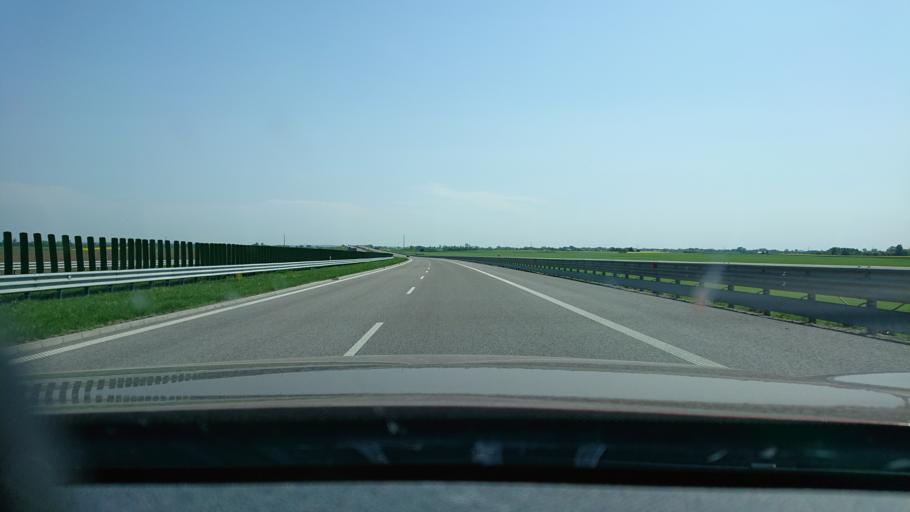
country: PL
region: Subcarpathian Voivodeship
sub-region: Powiat jaroslawski
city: Radymno
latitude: 49.9102
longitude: 22.8248
